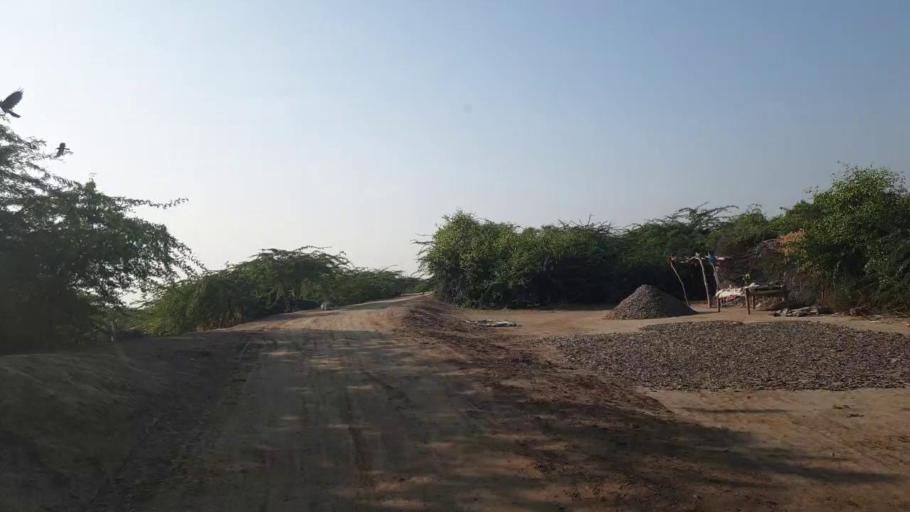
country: PK
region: Sindh
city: Badin
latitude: 24.4592
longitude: 68.7357
